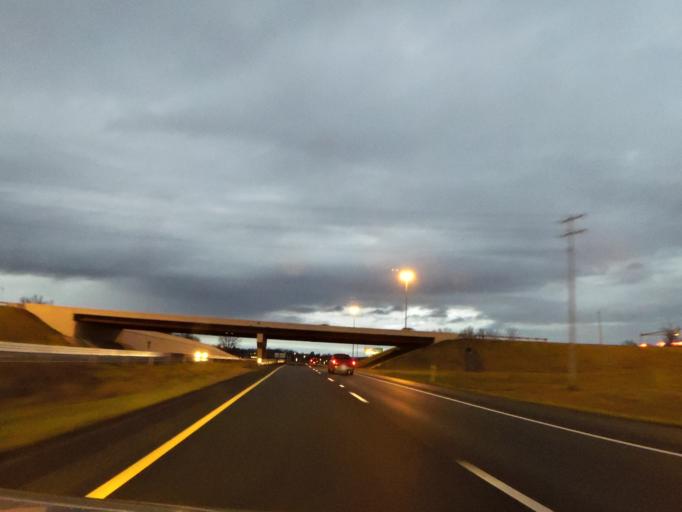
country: US
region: Tennessee
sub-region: Washington County
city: Gray
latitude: 36.4062
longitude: -82.4760
